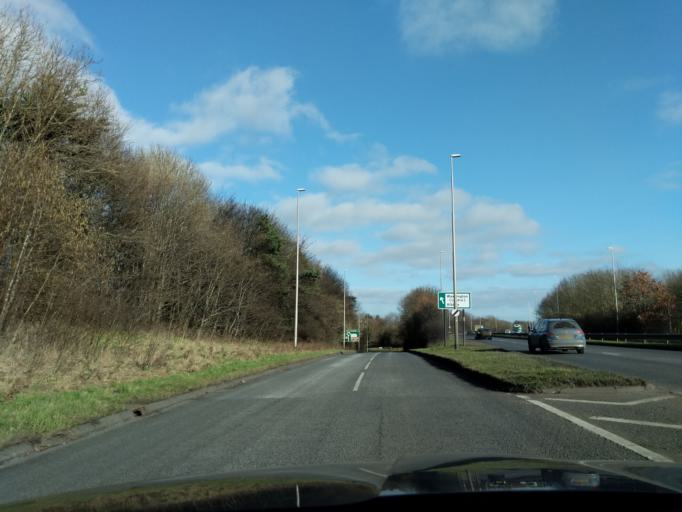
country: GB
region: England
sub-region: Sunderland
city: Washington
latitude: 54.9042
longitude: -1.5320
